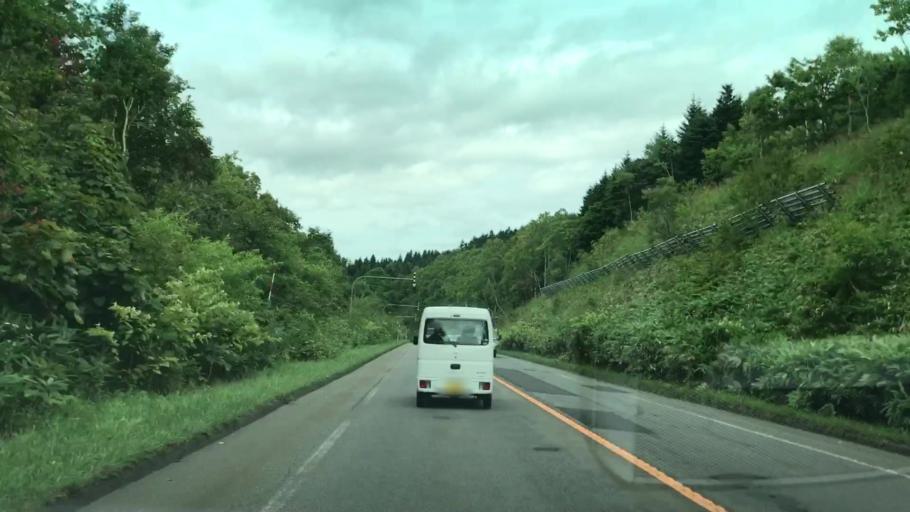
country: JP
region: Hokkaido
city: Niseko Town
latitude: 42.9306
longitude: 140.7133
